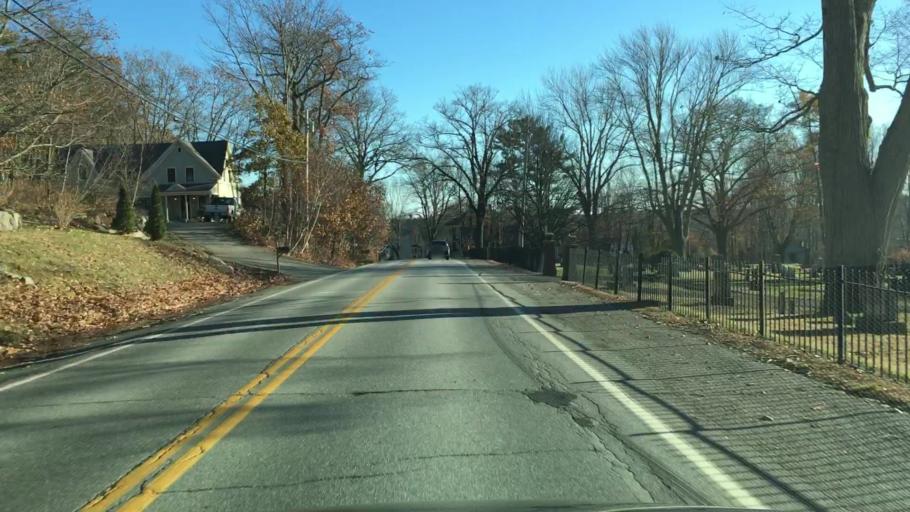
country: US
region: Maine
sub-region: Knox County
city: Camden
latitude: 44.2176
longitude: -69.0727
